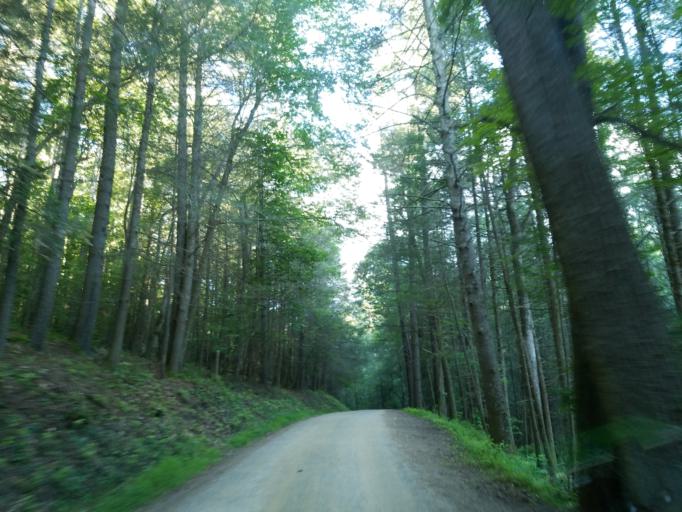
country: US
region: Georgia
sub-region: Union County
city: Blairsville
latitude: 34.7611
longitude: -84.0678
